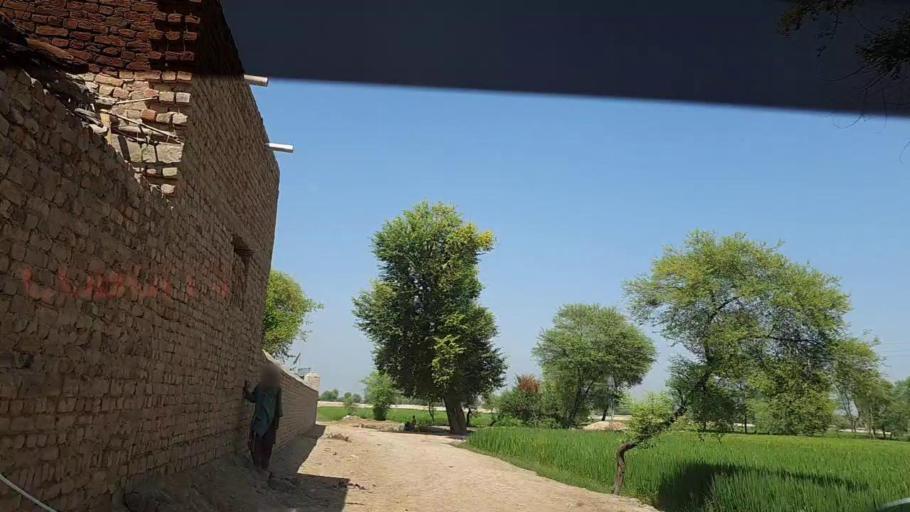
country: PK
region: Sindh
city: Tangwani
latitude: 28.2860
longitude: 69.0396
